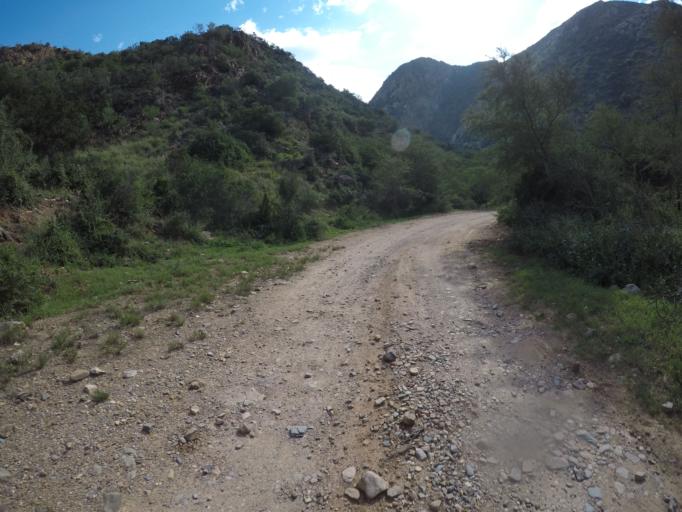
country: ZA
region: Eastern Cape
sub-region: Cacadu District Municipality
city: Kareedouw
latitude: -33.6375
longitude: 24.3217
